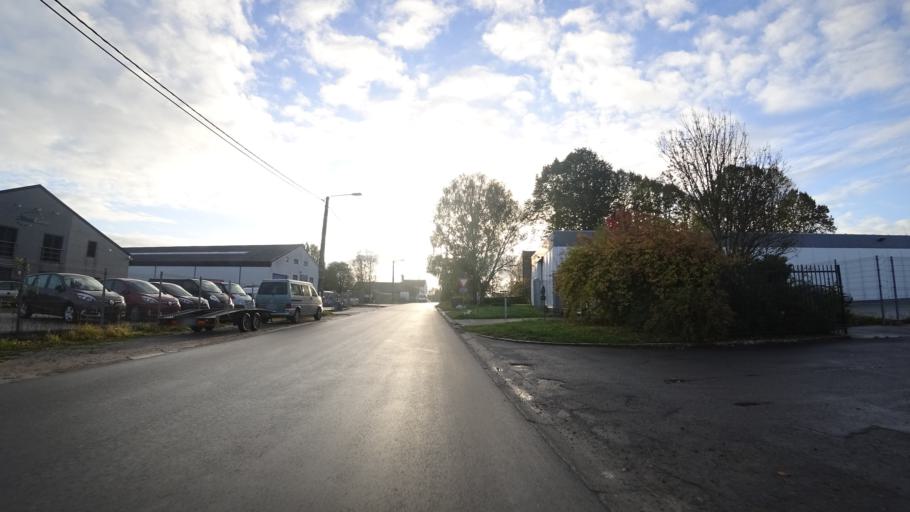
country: BE
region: Wallonia
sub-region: Province de Namur
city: Gembloux
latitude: 50.5833
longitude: 4.7089
